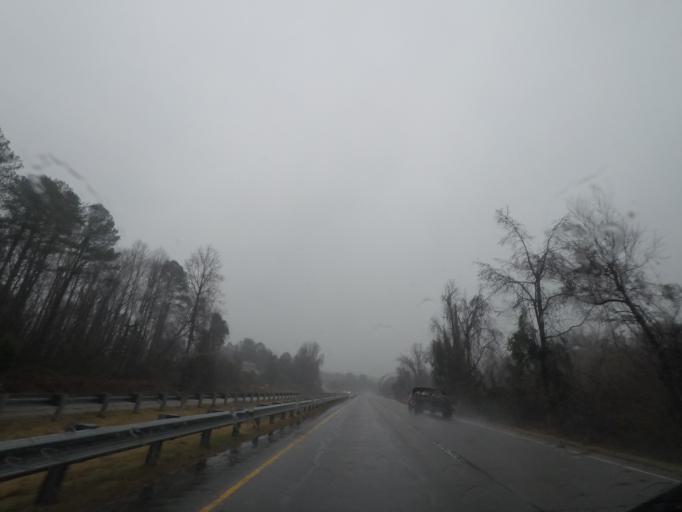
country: US
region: North Carolina
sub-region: Moore County
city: Southern Pines
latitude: 35.1830
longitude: -79.3946
